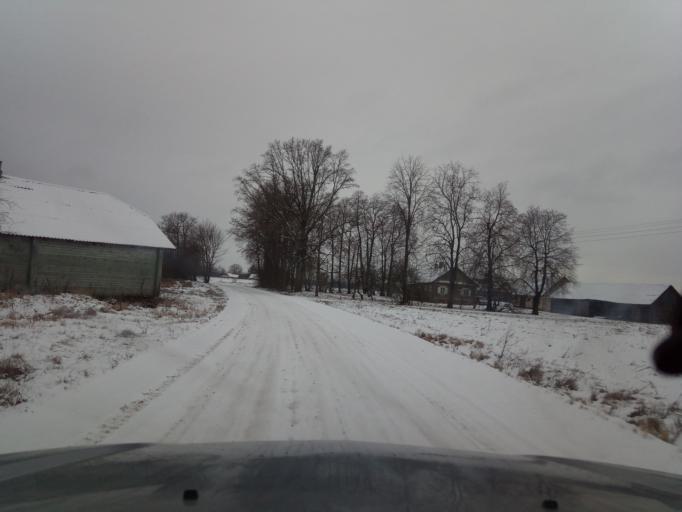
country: LT
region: Vilnius County
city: Ukmerge
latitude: 55.4861
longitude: 24.5899
